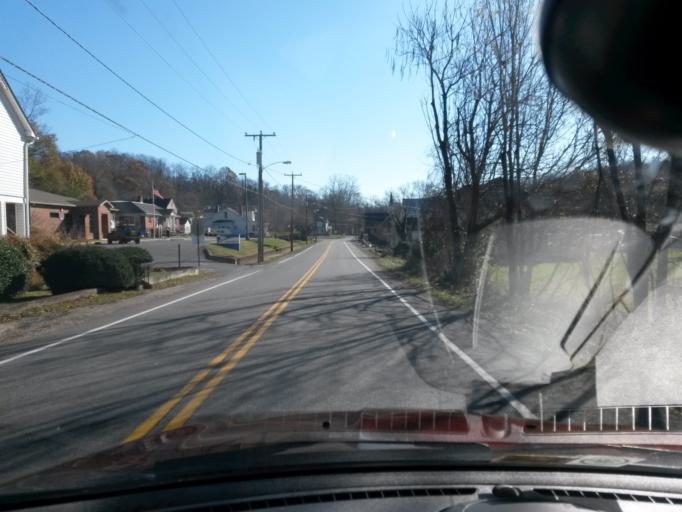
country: US
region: Virginia
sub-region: Botetourt County
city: Fincastle
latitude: 37.6397
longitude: -79.7999
